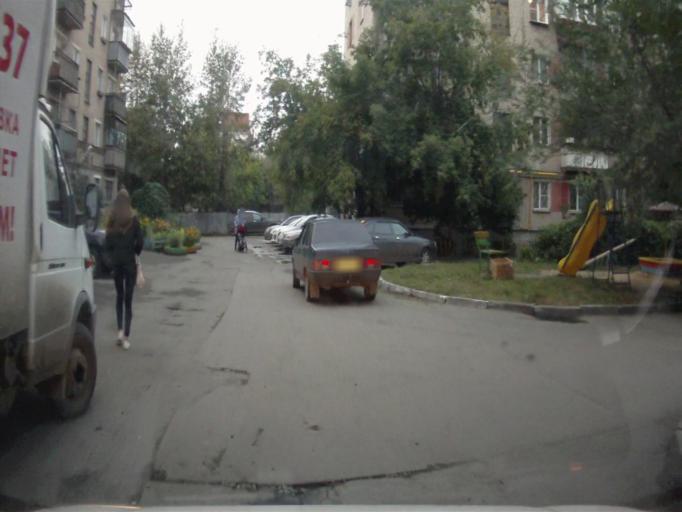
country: RU
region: Chelyabinsk
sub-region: Gorod Chelyabinsk
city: Chelyabinsk
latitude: 55.1454
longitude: 61.3858
